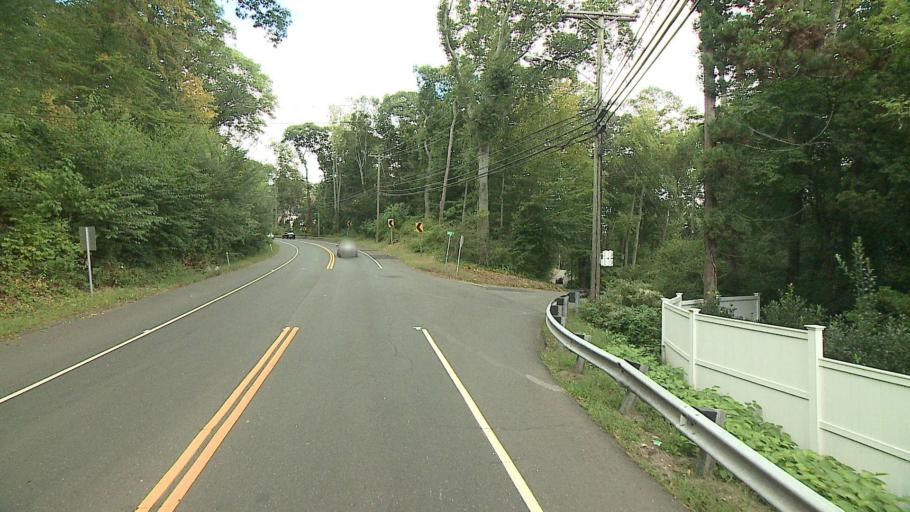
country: US
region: Connecticut
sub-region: Fairfield County
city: Westport
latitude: 41.1532
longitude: -73.3693
